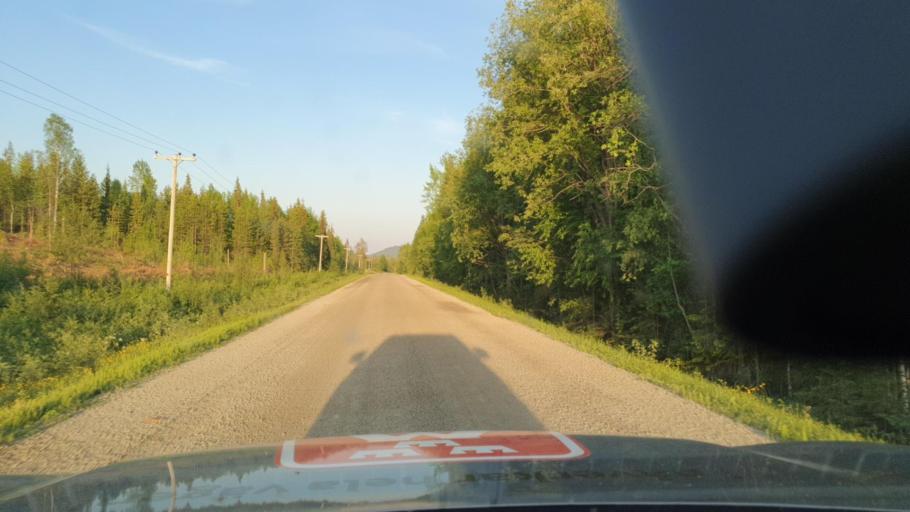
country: SE
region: Norrbotten
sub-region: Bodens Kommun
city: Boden
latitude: 66.1742
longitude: 21.5195
